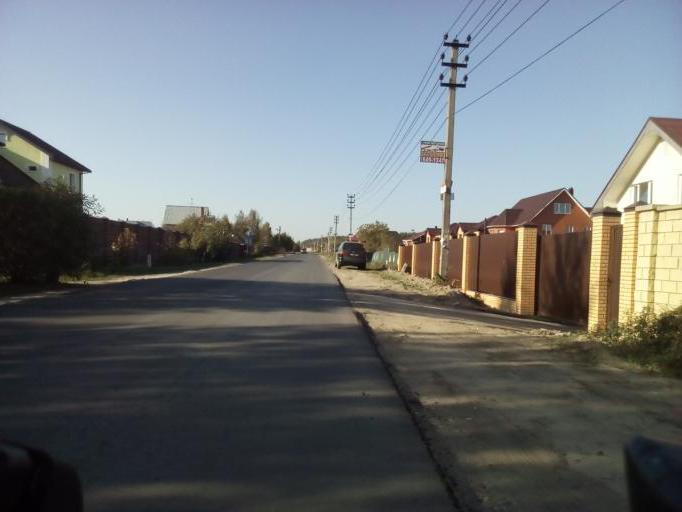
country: RU
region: Moskovskaya
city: Malyshevo
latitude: 55.5561
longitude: 38.3120
